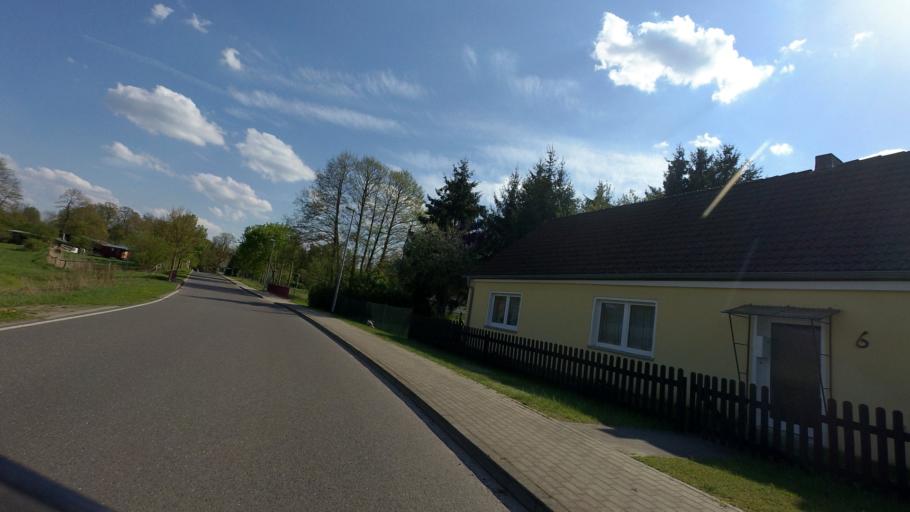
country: DE
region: Brandenburg
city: Templin
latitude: 53.0544
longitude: 13.5266
